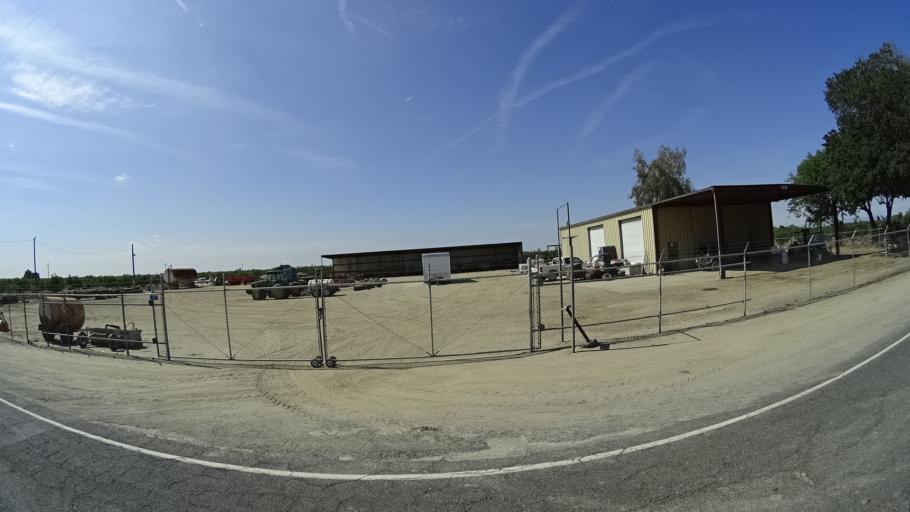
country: US
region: California
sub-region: Kings County
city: Armona
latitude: 36.2548
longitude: -119.7331
